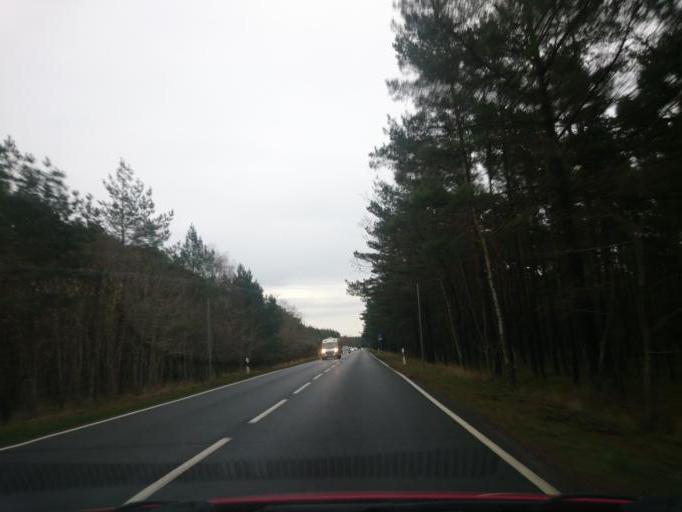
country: DE
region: Mecklenburg-Vorpommern
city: Glowe
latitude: 54.5730
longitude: 13.4271
